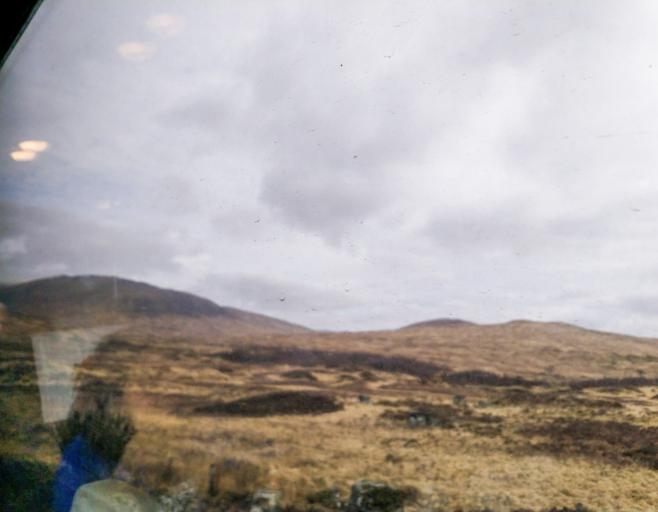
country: GB
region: Scotland
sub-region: Highland
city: Spean Bridge
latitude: 56.6937
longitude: -4.5733
